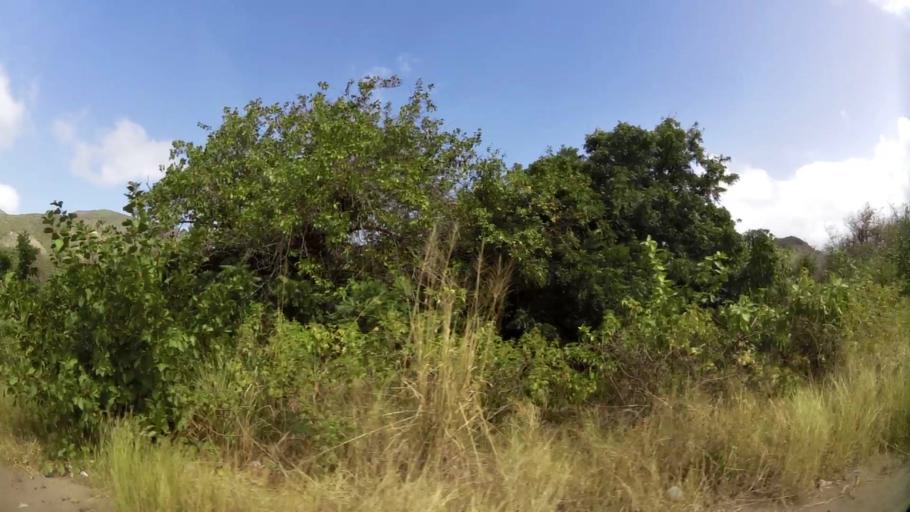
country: KN
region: Saint James Windwa
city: Newcastle
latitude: 17.2309
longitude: -62.6361
